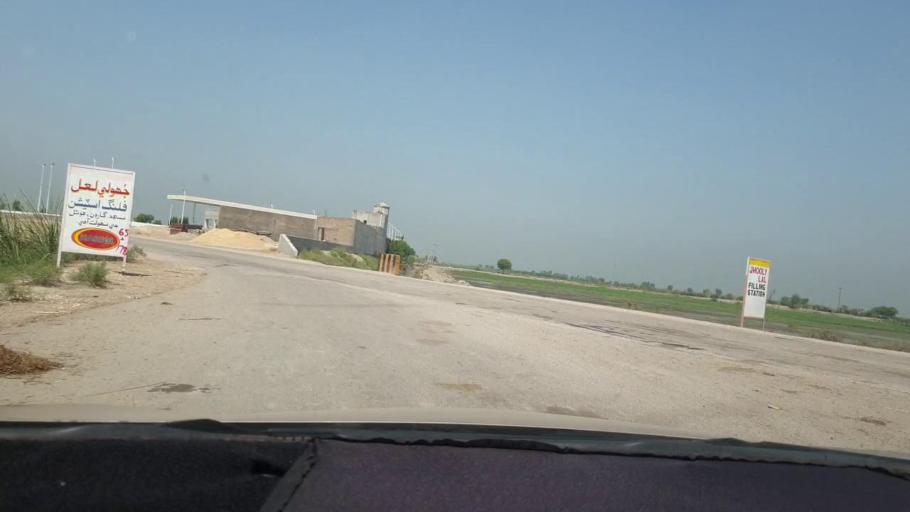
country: PK
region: Sindh
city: Shahdadkot
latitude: 27.8467
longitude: 67.9997
